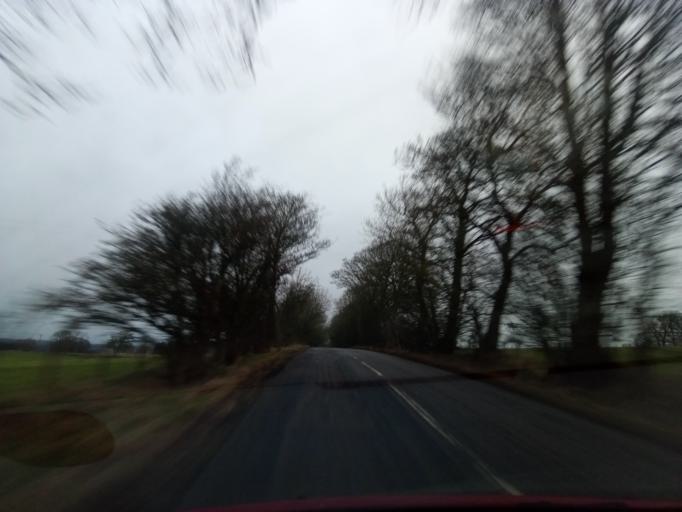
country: GB
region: England
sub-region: Northumberland
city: Rothley
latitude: 55.1947
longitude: -1.9719
